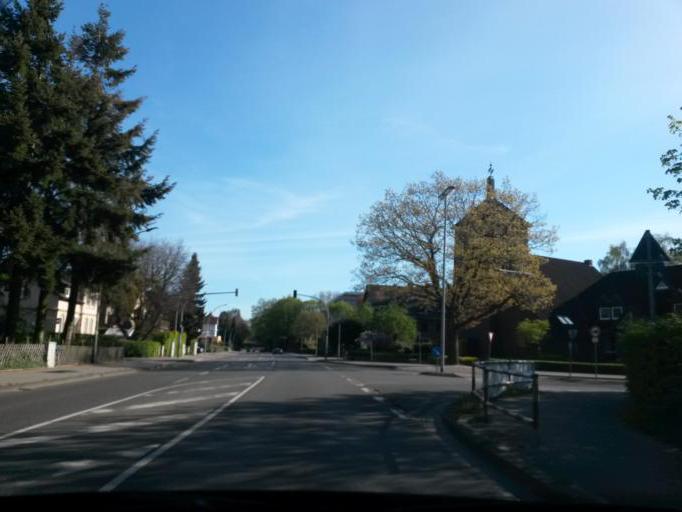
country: DE
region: Schleswig-Holstein
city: Halstenbek
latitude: 53.6283
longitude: 9.8349
